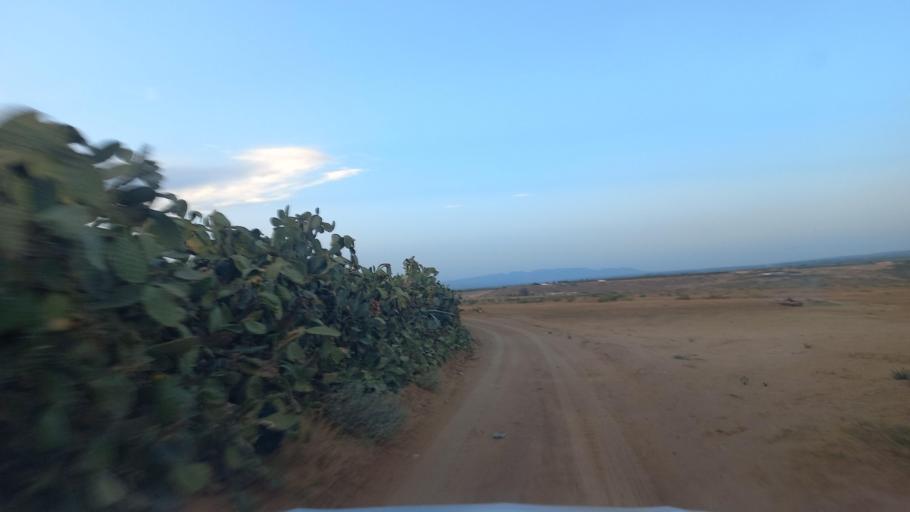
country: TN
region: Al Qasrayn
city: Kasserine
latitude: 35.1973
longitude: 9.0505
